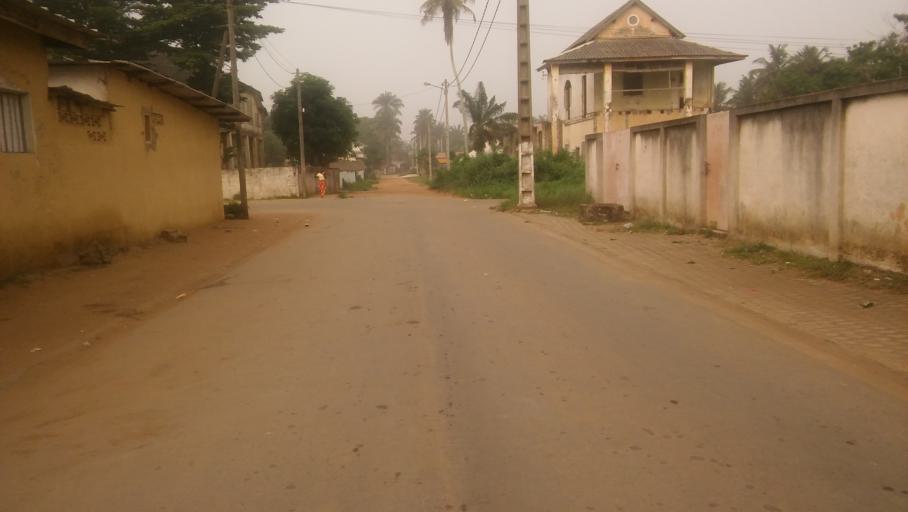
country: CI
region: Sud-Comoe
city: Grand-Bassam
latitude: 5.1972
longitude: -3.7387
